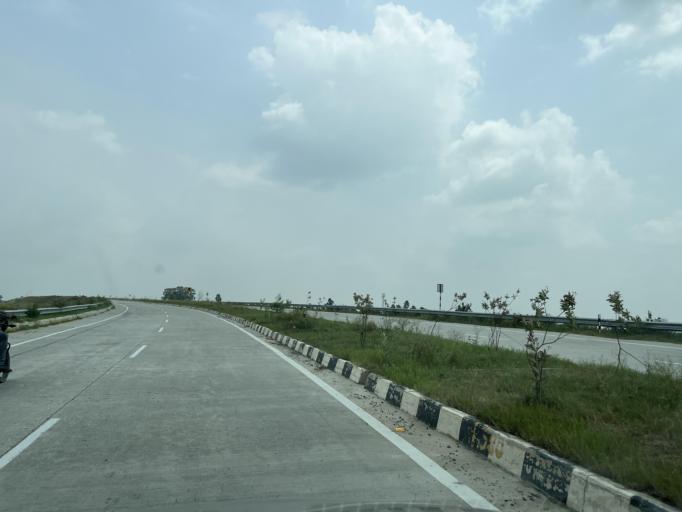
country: IN
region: Uttar Pradesh
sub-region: Bijnor
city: Nagina
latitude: 29.4249
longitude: 78.4252
